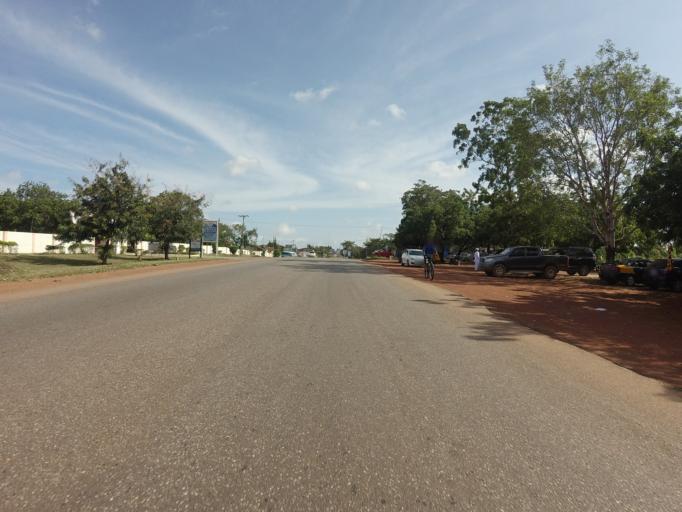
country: GH
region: Greater Accra
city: Medina Estates
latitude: 5.6539
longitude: -0.1693
